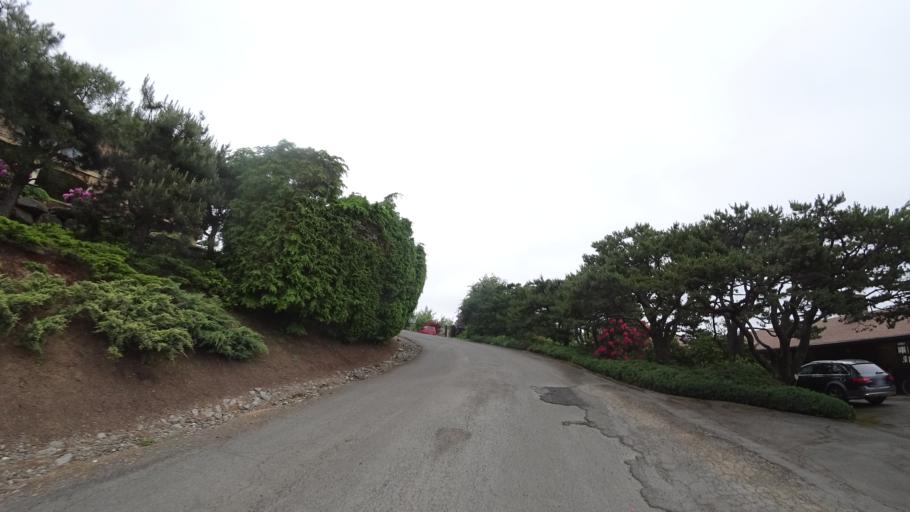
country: US
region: Oregon
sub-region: Multnomah County
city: Portland
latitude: 45.4880
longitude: -122.6912
